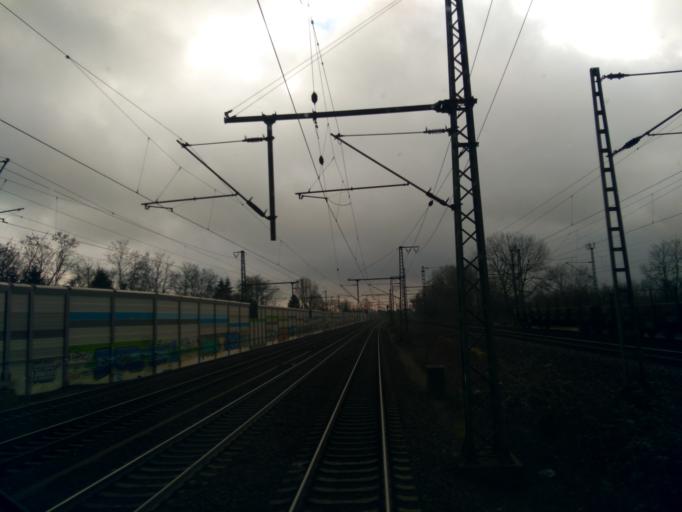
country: DE
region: Hamburg
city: Harburg
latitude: 53.4812
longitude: 10.0023
